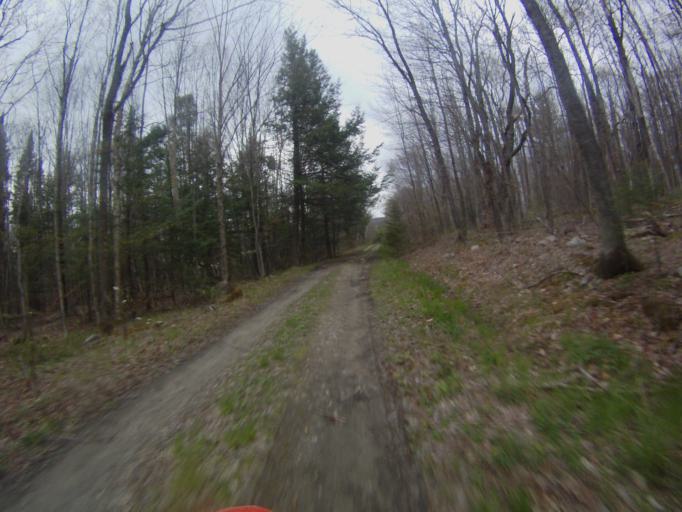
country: US
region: Vermont
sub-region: Addison County
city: Bristol
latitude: 44.0521
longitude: -73.0506
